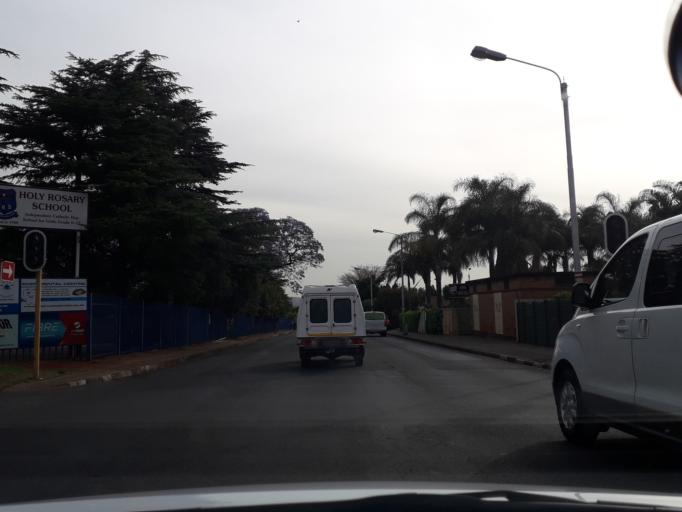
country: ZA
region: Gauteng
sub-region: City of Johannesburg Metropolitan Municipality
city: Modderfontein
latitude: -26.1521
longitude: 28.1547
